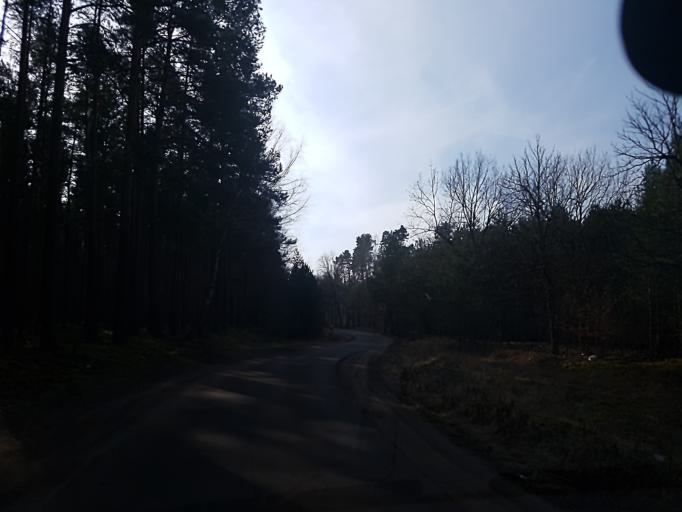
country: DE
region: Brandenburg
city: Wenzlow
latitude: 52.3523
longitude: 12.4651
